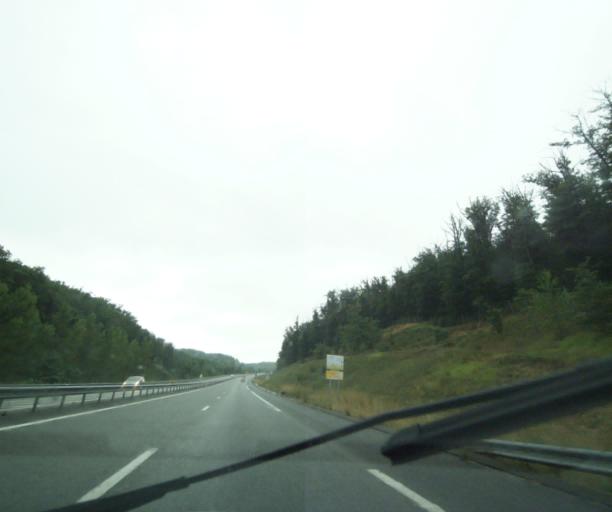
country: FR
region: Midi-Pyrenees
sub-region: Departement du Tarn
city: Le Garric
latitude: 43.9967
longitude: 2.1716
